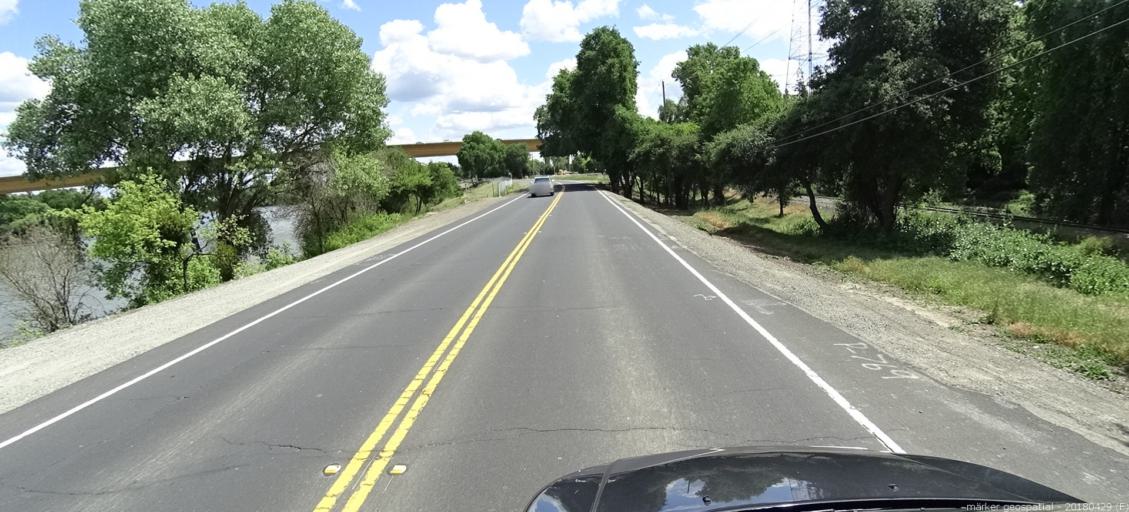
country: US
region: California
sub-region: Yolo County
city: West Sacramento
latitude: 38.5990
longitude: -121.5514
